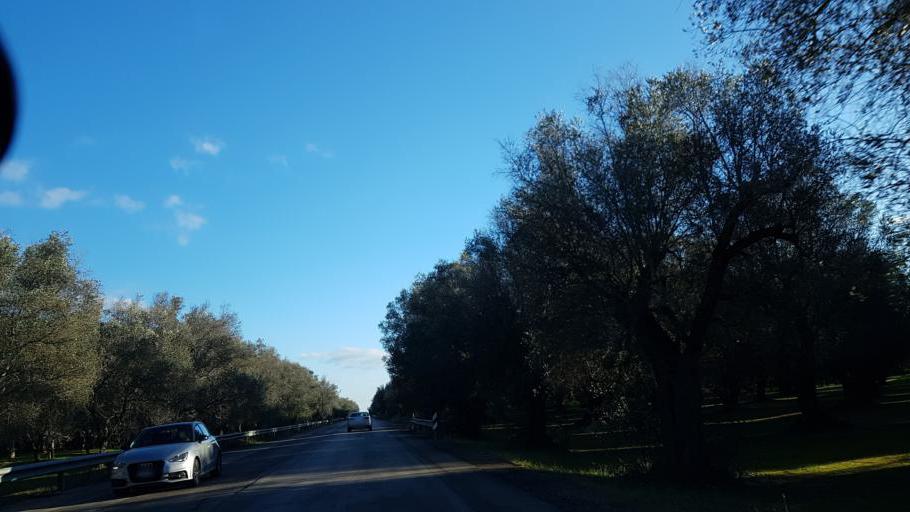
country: IT
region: Apulia
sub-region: Provincia di Brindisi
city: San Pietro Vernotico
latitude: 40.4683
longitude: 18.0146
